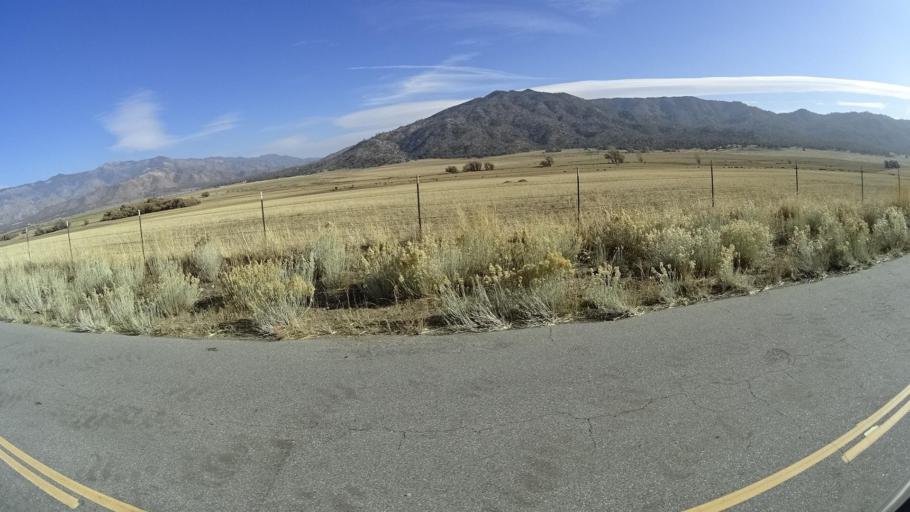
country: US
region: California
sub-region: Kern County
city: Bodfish
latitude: 35.3994
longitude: -118.5465
